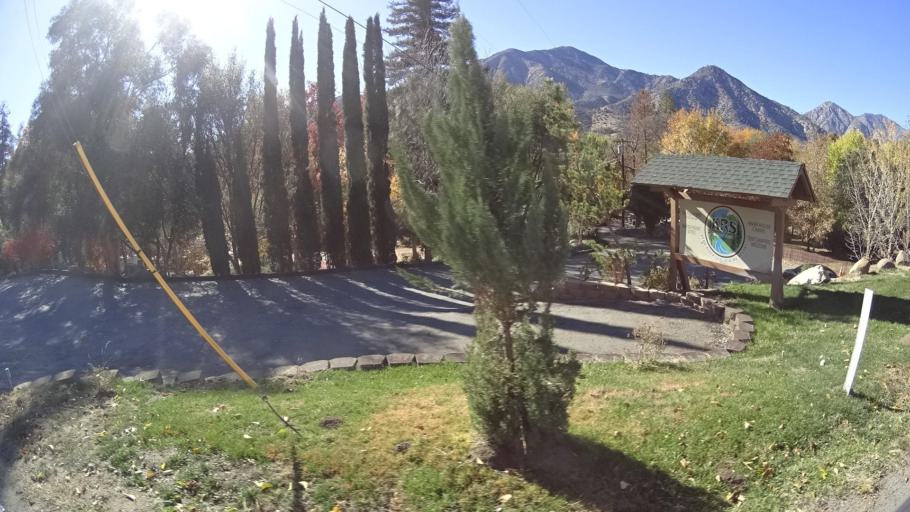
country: US
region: California
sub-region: Kern County
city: Kernville
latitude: 35.7629
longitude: -118.4216
